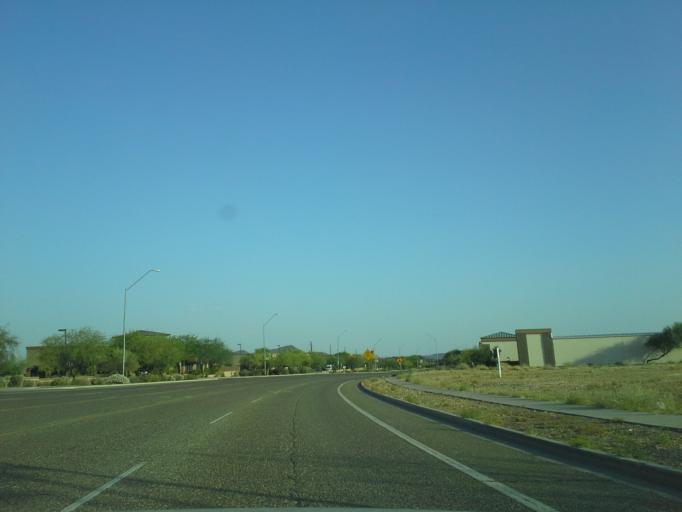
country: US
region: Arizona
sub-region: Maricopa County
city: Anthem
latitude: 33.8679
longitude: -112.1508
